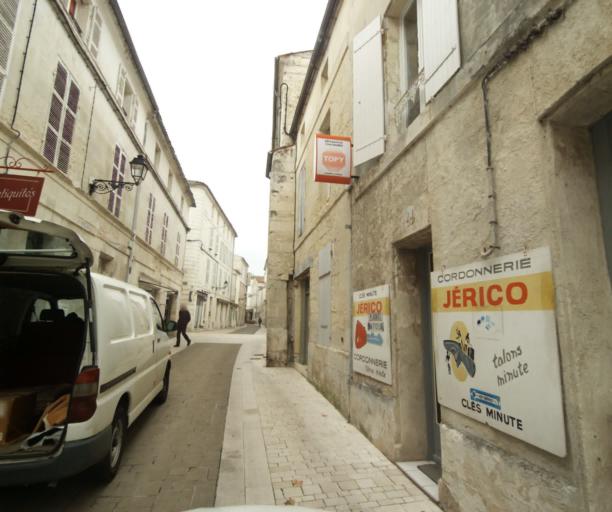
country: FR
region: Poitou-Charentes
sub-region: Departement de la Charente-Maritime
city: Saintes
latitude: 45.7453
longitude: -0.6316
